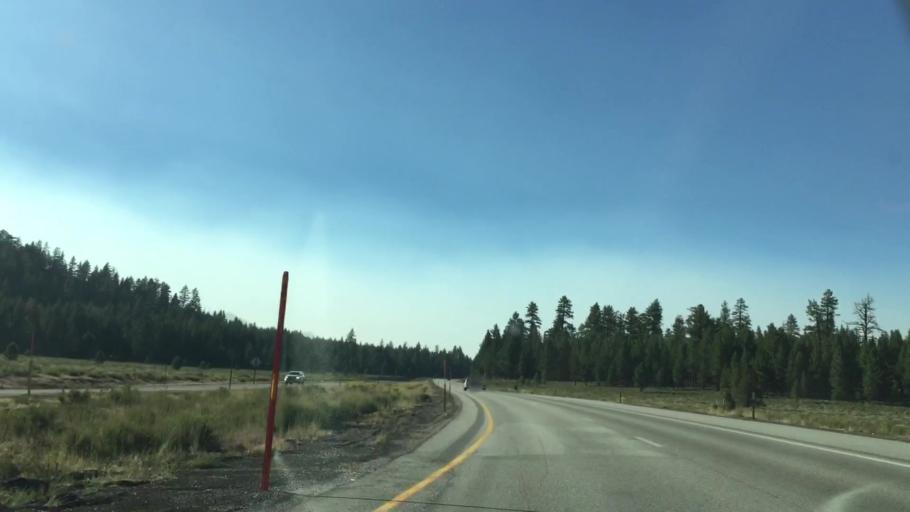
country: US
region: California
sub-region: Mono County
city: Mammoth Lakes
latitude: 37.6920
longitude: -118.9439
